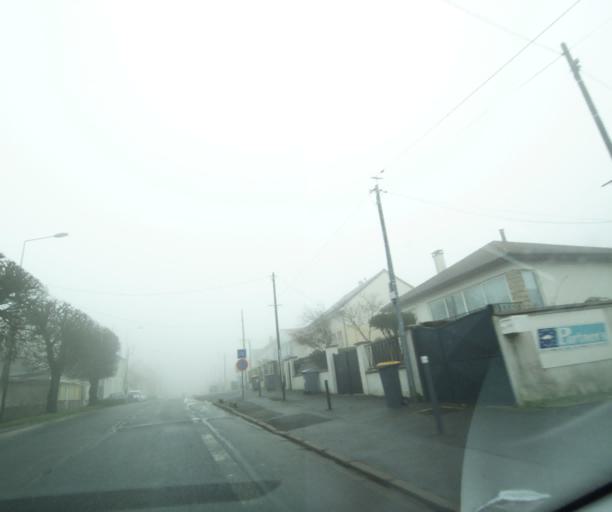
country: FR
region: Ile-de-France
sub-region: Departement de Seine-et-Marne
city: Dammartin-en-Goele
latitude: 49.0533
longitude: 2.6897
